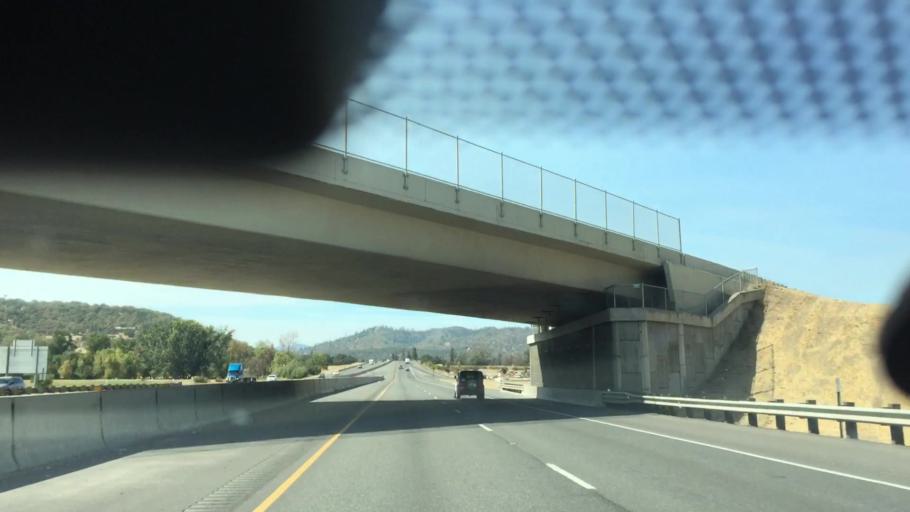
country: US
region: Oregon
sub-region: Jackson County
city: Central Point
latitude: 42.4066
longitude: -122.9423
